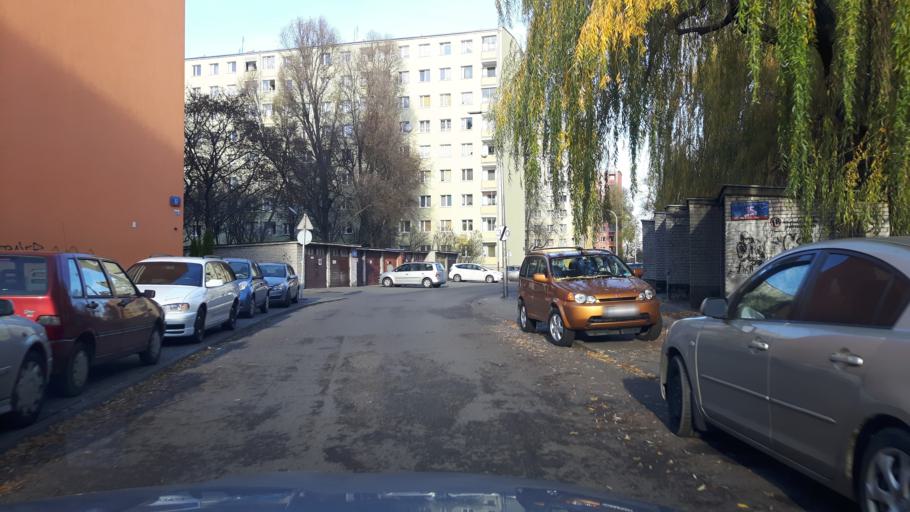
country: PL
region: Masovian Voivodeship
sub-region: Warszawa
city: Ochota
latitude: 52.2034
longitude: 20.9719
